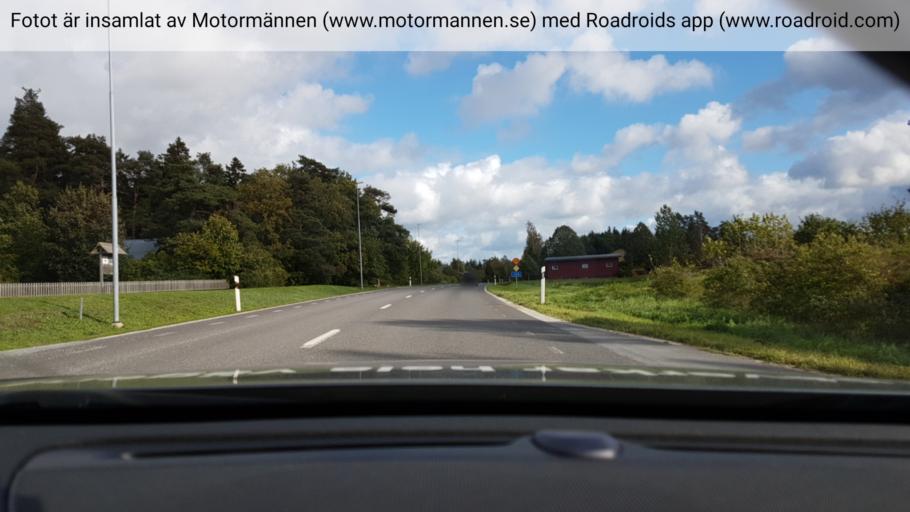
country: SE
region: Gotland
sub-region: Gotland
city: Visby
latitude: 57.4965
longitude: 18.4755
